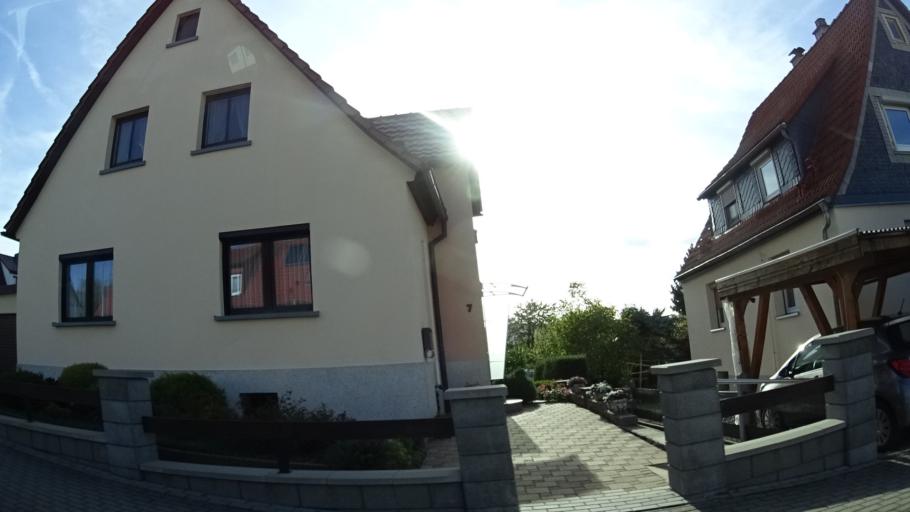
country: DE
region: Thuringia
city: Zella-Mehlis
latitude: 50.6635
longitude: 10.6758
